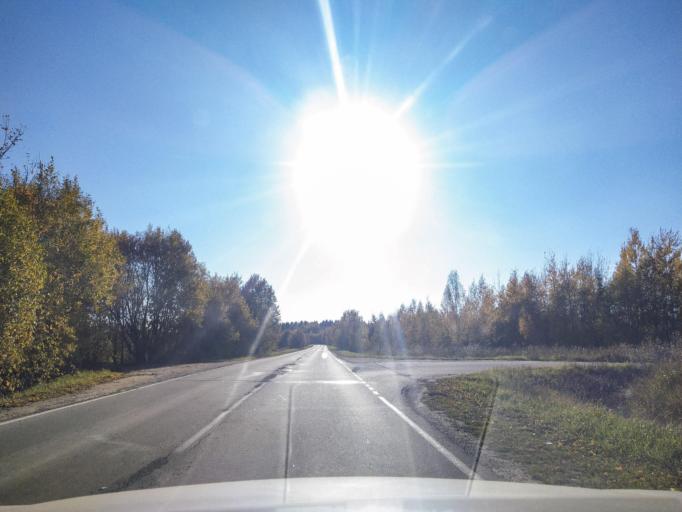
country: RU
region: Leningrad
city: Siverskiy
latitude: 59.3129
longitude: 30.0326
